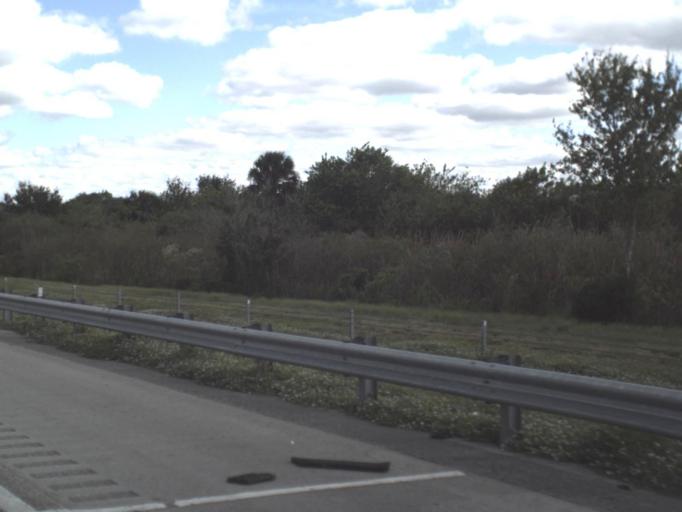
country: US
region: Florida
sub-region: Indian River County
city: Fellsmere
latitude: 27.5593
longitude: -80.7309
